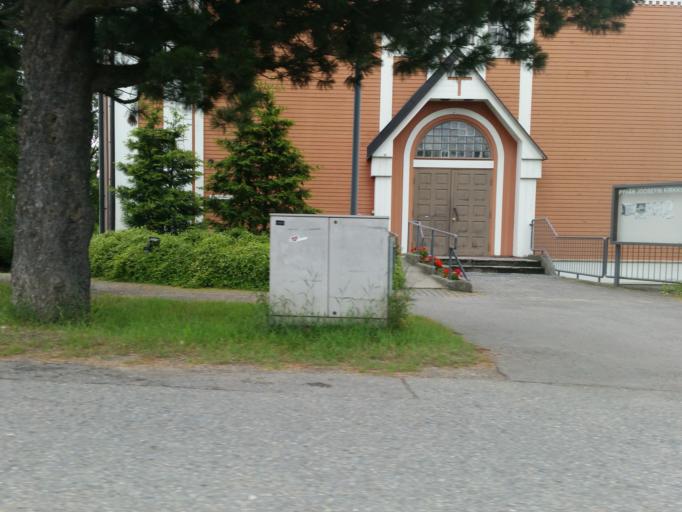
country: FI
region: Northern Savo
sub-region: Kuopio
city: Kuopio
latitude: 62.9012
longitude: 27.7057
